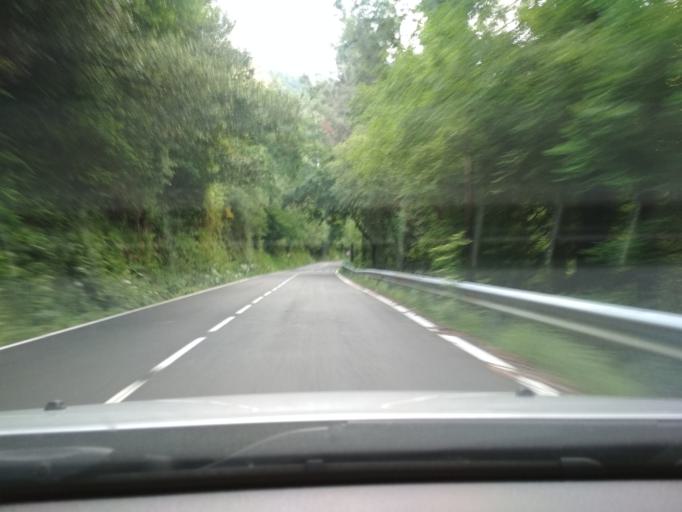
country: ES
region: Galicia
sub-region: Provincia da Coruna
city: Outes
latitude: 42.8926
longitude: -8.9300
